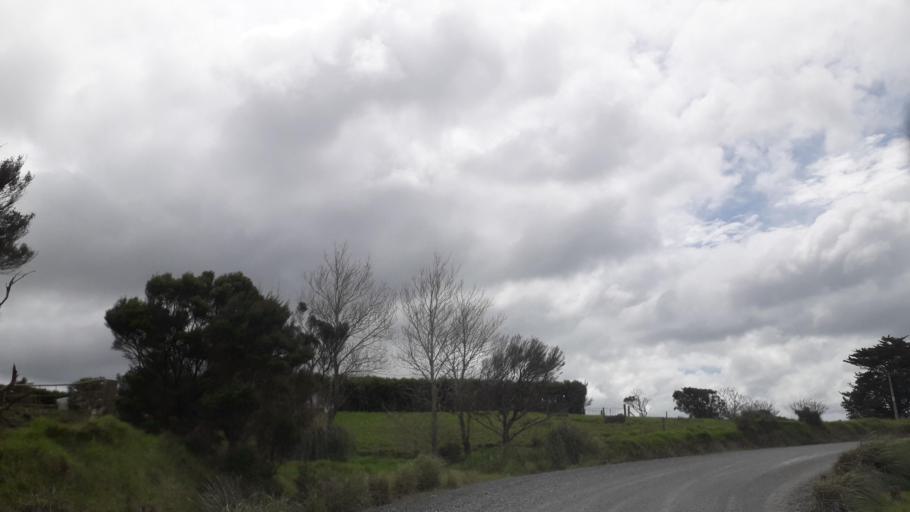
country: NZ
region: Northland
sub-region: Far North District
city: Taipa
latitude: -35.0022
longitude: 173.4309
